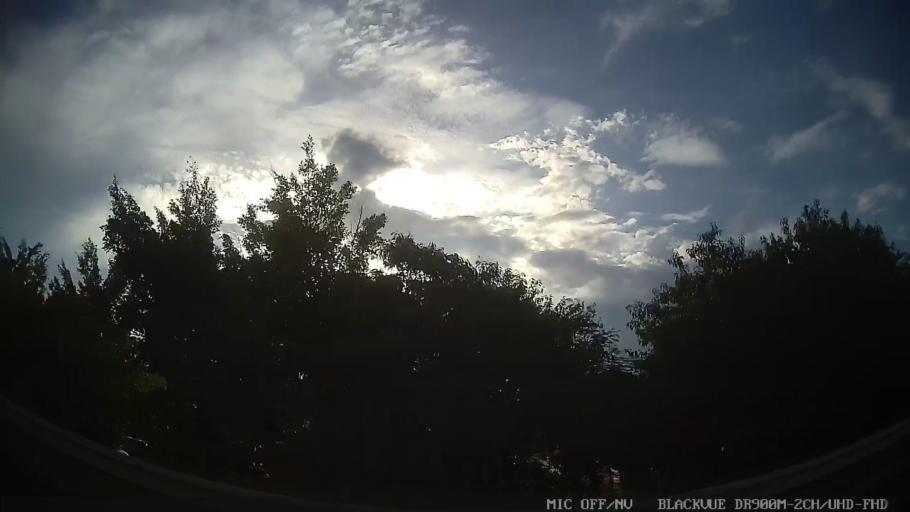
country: BR
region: Sao Paulo
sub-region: Tiete
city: Tiete
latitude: -23.1029
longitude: -47.7247
